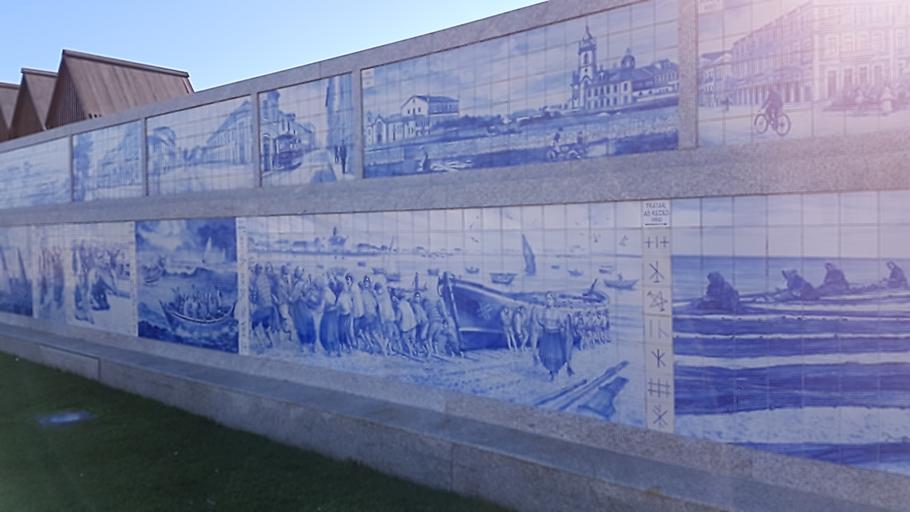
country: PT
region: Porto
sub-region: Povoa de Varzim
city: Povoa de Varzim
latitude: 41.3781
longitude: -8.7677
